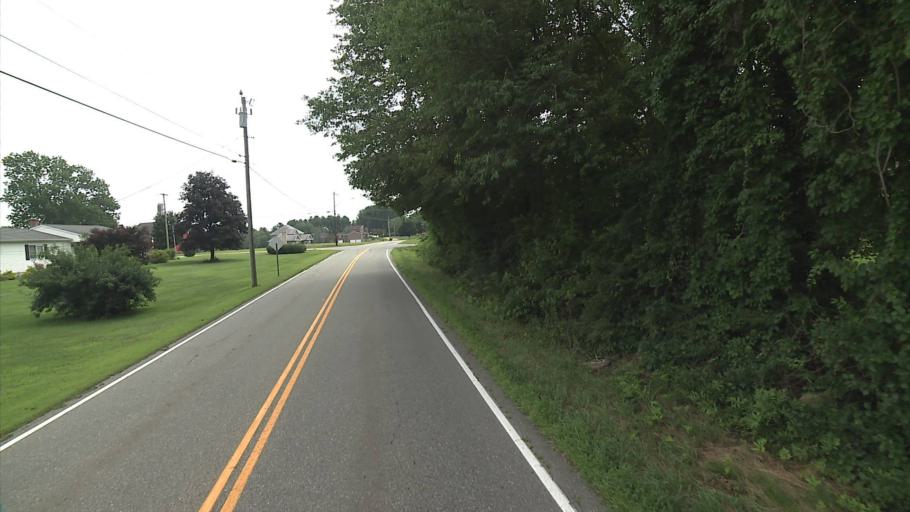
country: US
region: Connecticut
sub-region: Windham County
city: Wauregan
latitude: 41.7590
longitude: -71.9267
